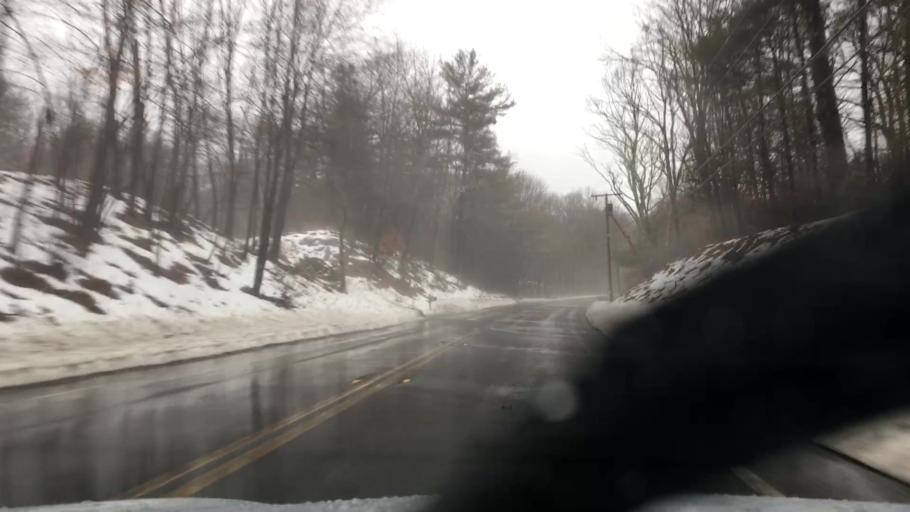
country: US
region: Massachusetts
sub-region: Hampshire County
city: Belchertown
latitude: 42.3211
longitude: -72.4063
